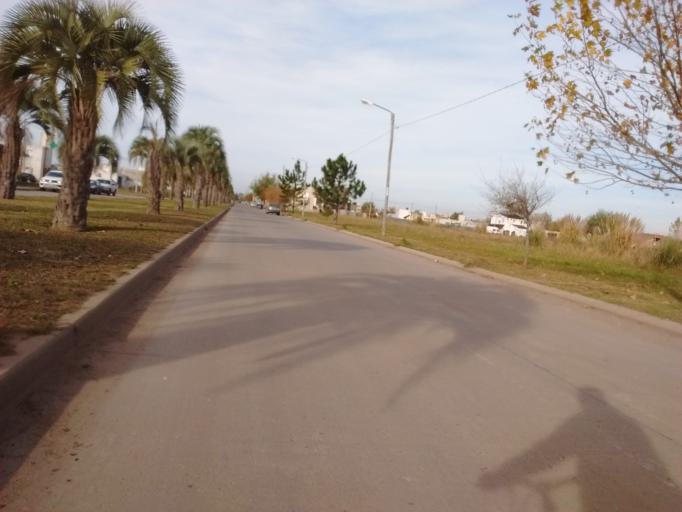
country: AR
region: Santa Fe
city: Roldan
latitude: -32.9317
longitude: -60.8968
